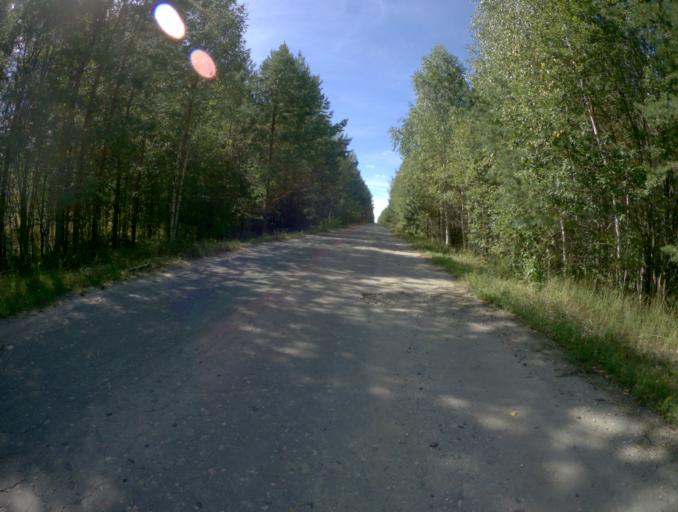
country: RU
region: Vladimir
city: Zolotkovo
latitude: 55.5989
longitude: 41.1911
